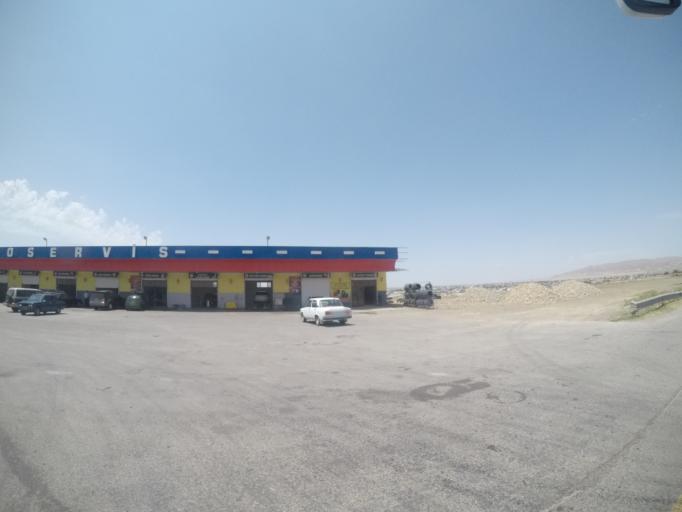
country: AZ
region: Haciqabul
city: Haciqabul
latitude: 40.0206
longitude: 48.9548
